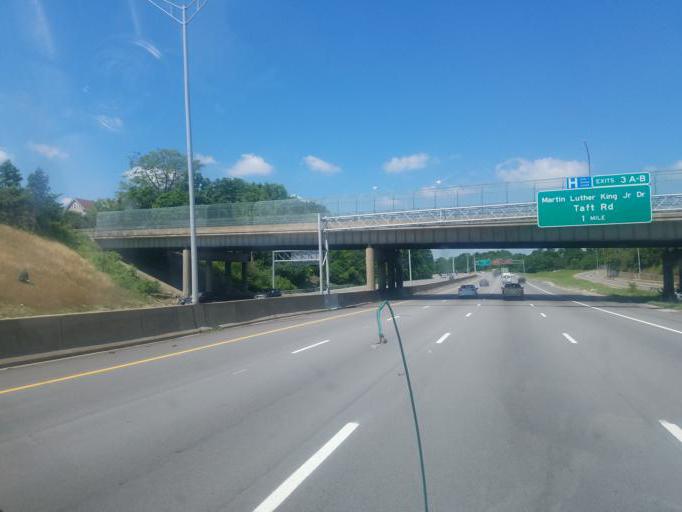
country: US
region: Ohio
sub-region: Hamilton County
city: Norwood
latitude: 39.1437
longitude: -84.4741
